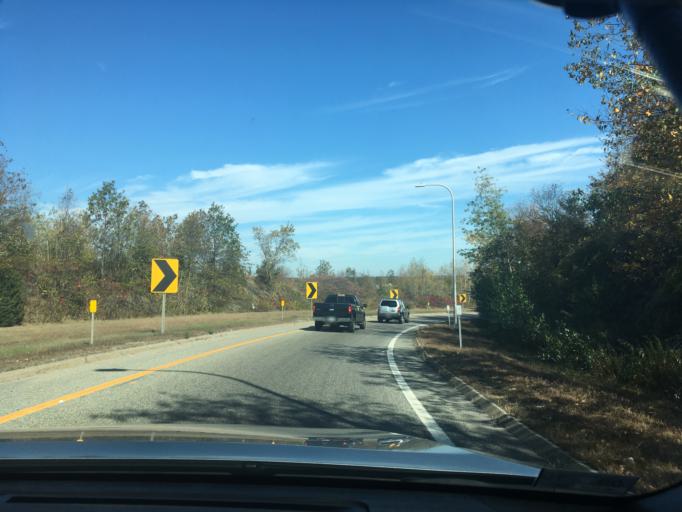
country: US
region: Rhode Island
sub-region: Providence County
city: Johnston
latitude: 41.8188
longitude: -71.5106
